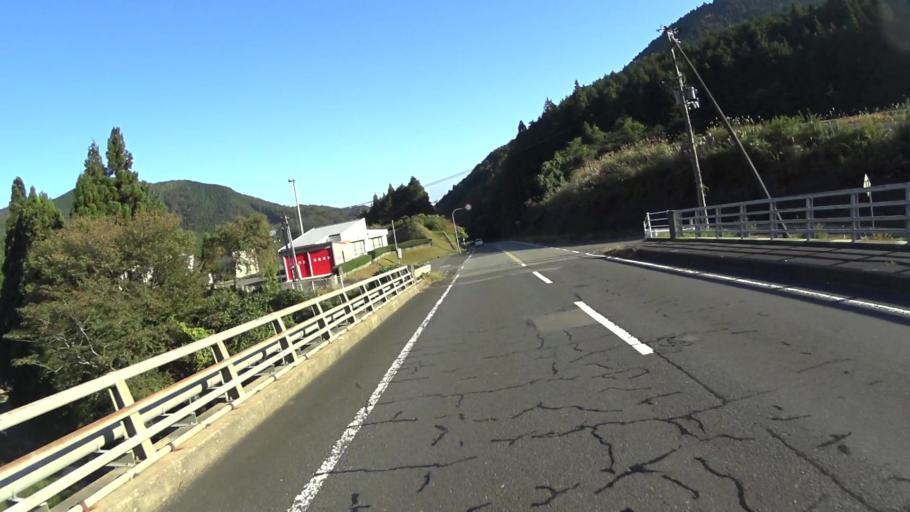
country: JP
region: Kyoto
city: Fukuchiyama
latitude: 35.3994
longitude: 135.0834
